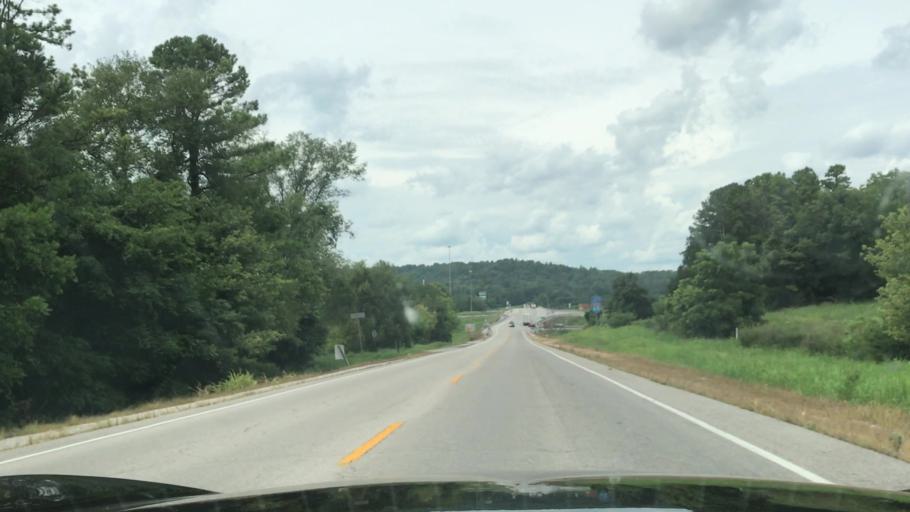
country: US
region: Kentucky
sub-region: Hart County
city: Horse Cave
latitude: 37.1982
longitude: -85.9323
